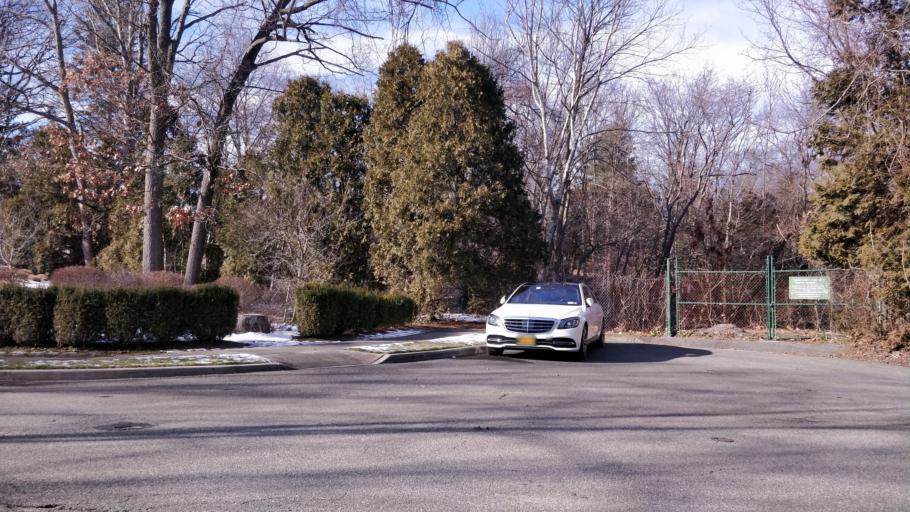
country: US
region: New York
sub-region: Nassau County
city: East Norwich
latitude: 40.8524
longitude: -73.5262
